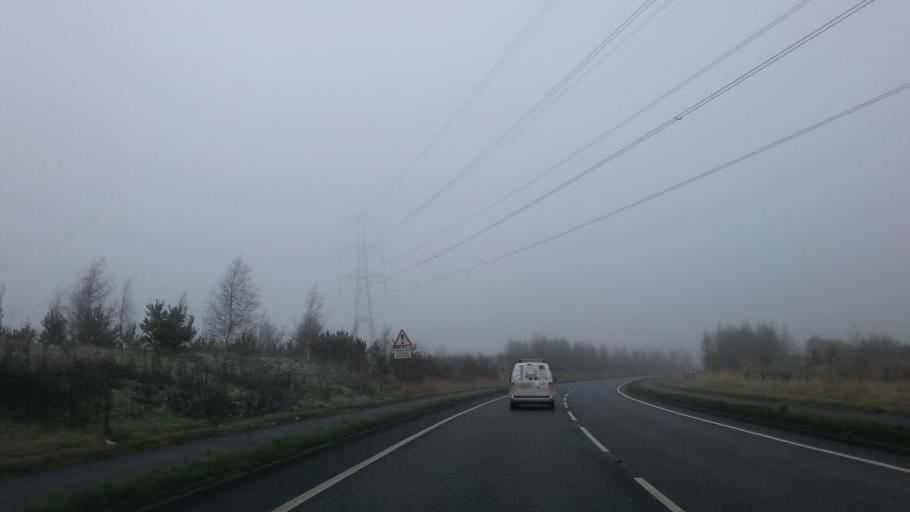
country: GB
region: England
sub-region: Cheshire East
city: Alderley Edge
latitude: 53.2922
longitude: -2.2556
